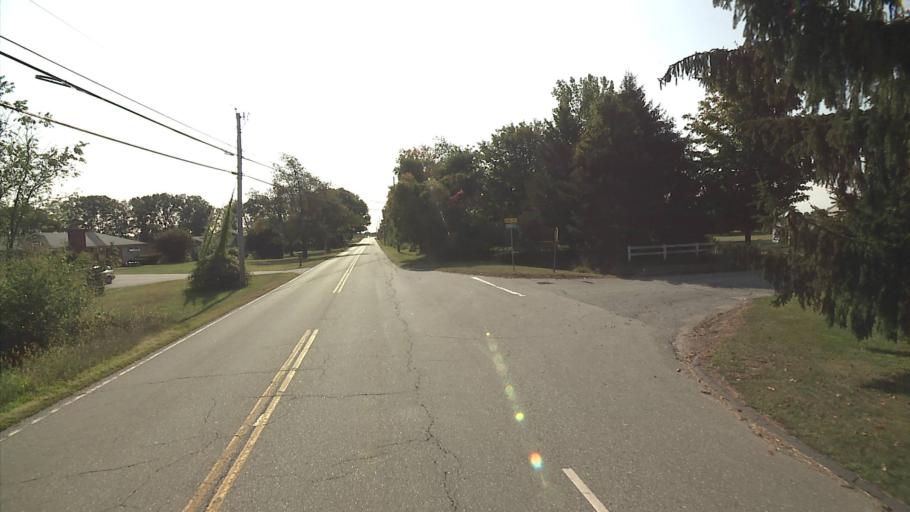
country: US
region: Connecticut
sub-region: Windham County
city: South Windham
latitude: 41.6067
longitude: -72.1732
